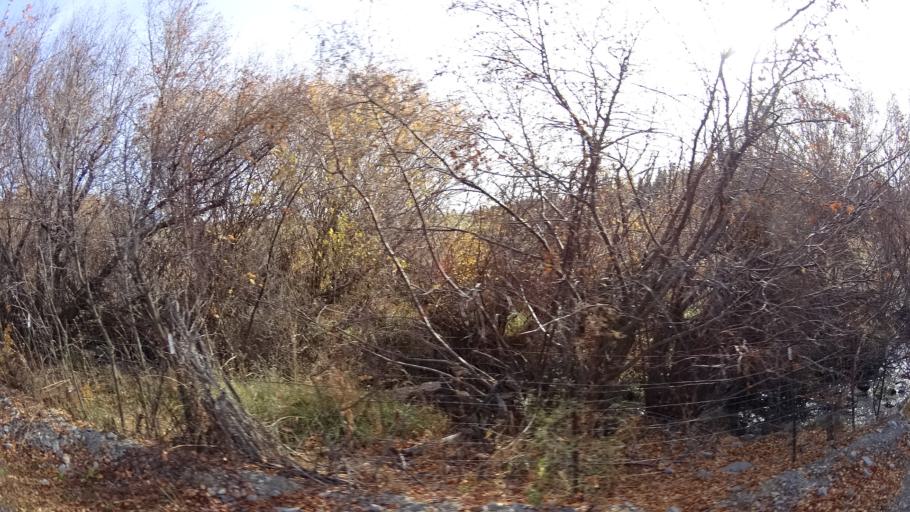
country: US
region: California
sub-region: Siskiyou County
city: Weed
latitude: 41.4650
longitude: -122.3929
